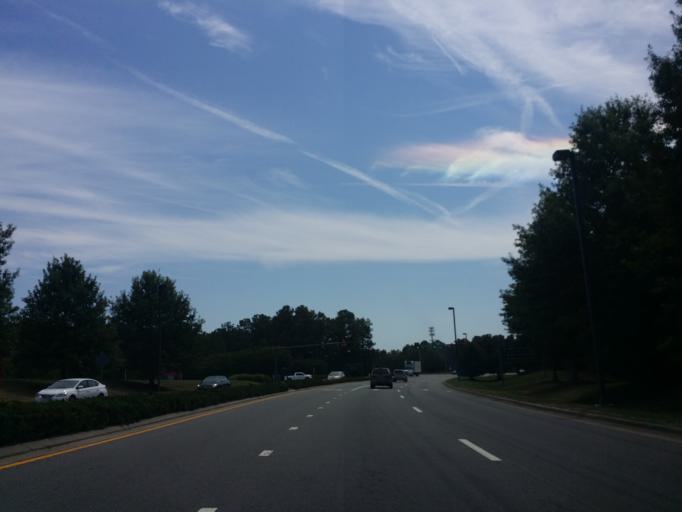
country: US
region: North Carolina
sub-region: Wake County
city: Morrisville
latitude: 35.8559
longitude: -78.7966
